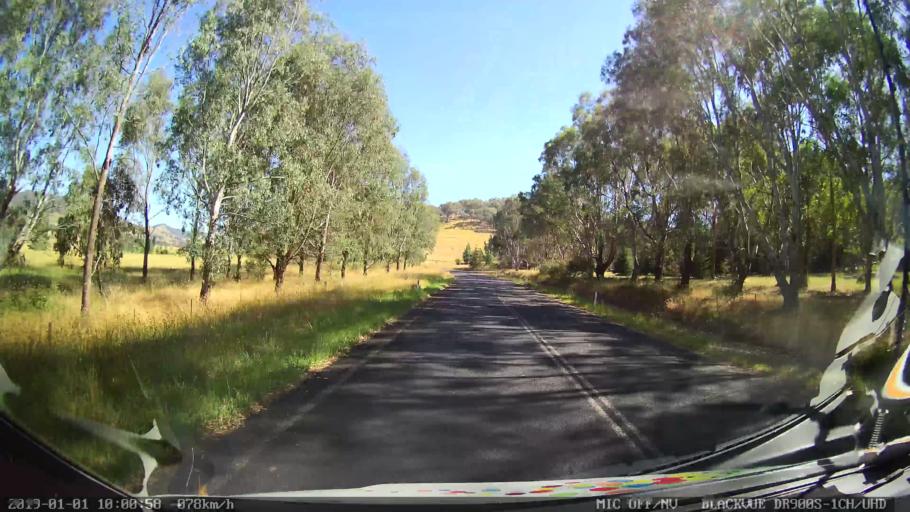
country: AU
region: New South Wales
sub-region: Snowy River
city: Jindabyne
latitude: -36.1964
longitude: 148.1030
